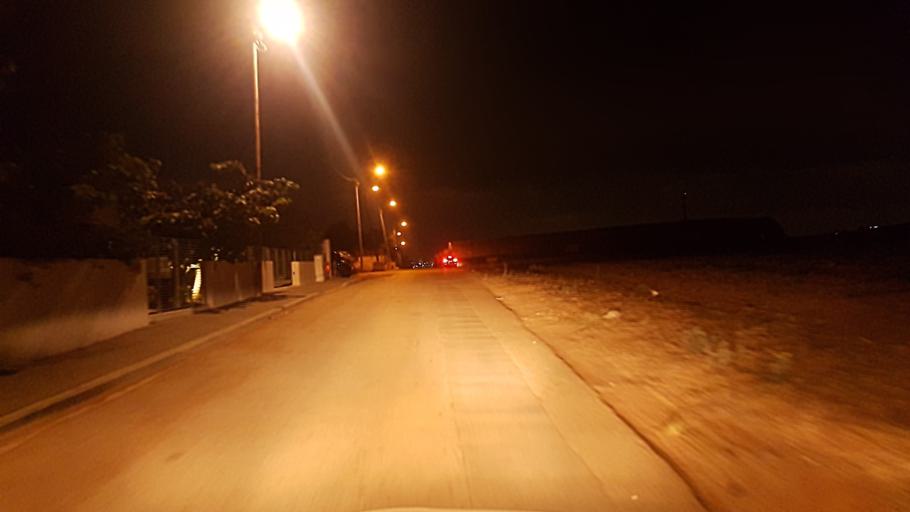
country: IL
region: Central District
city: Hod HaSharon
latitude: 32.1595
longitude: 34.8722
